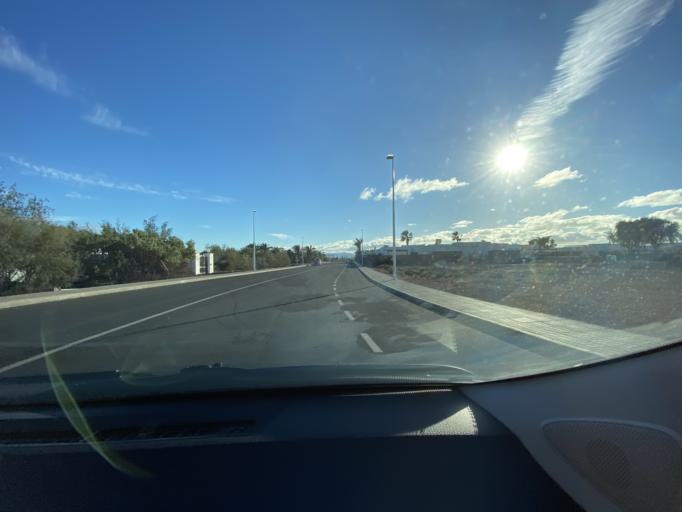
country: ES
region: Canary Islands
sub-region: Provincia de Las Palmas
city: Playa Blanca
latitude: 28.8652
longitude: -13.8412
